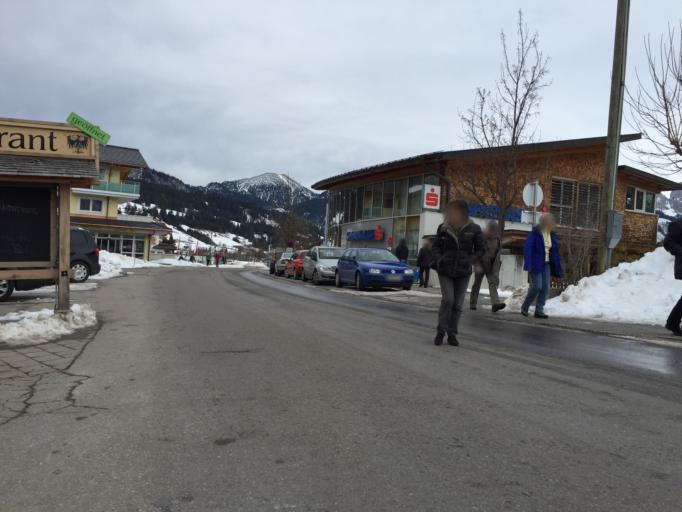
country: AT
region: Tyrol
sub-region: Politischer Bezirk Reutte
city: Tannheim
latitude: 47.4983
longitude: 10.5200
